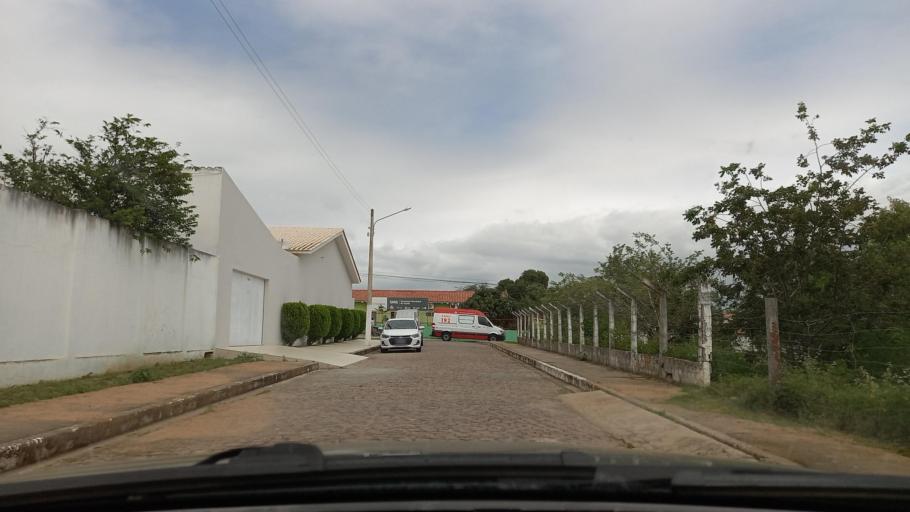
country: BR
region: Sergipe
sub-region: Caninde De Sao Francisco
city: Caninde de Sao Francisco
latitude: -9.6140
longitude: -37.7651
